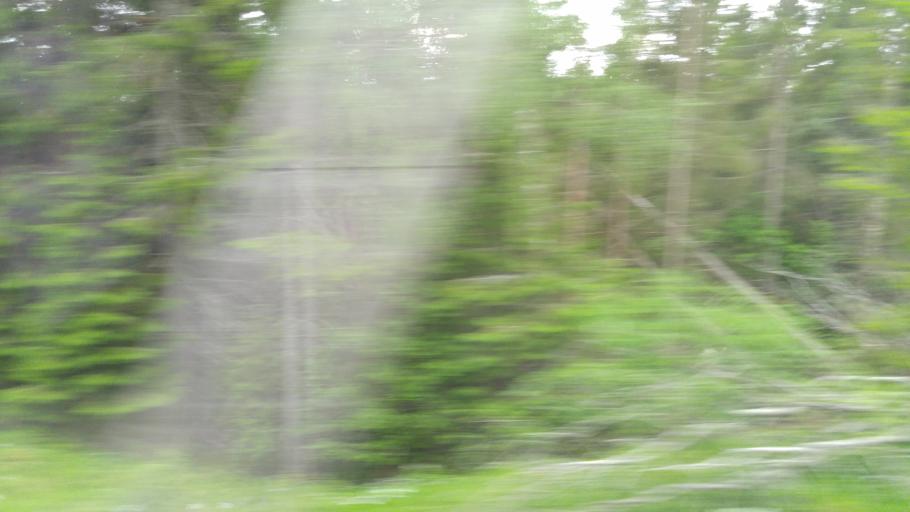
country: NO
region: Nord-Trondelag
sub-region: Meraker
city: Meraker
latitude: 63.4067
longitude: 11.7663
